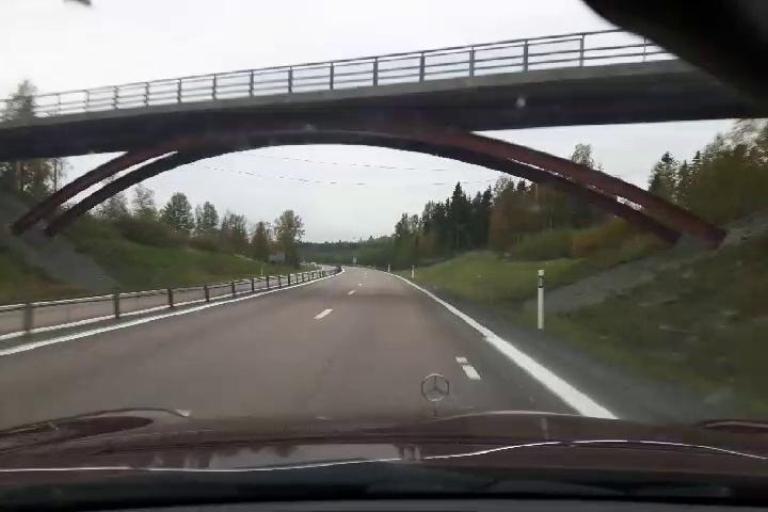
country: SE
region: Vaesternorrland
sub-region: Haernoesands Kommun
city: Haernoesand
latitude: 62.8690
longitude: 18.0400
